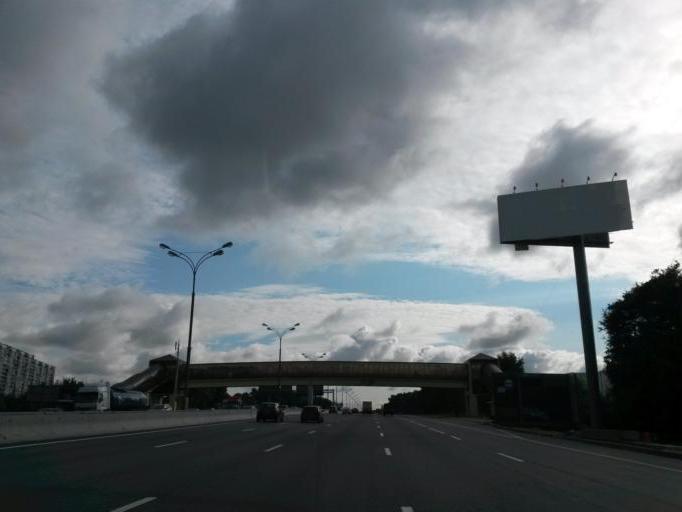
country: RU
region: Moskovskaya
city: Razvilka
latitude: 55.5969
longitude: 37.7419
